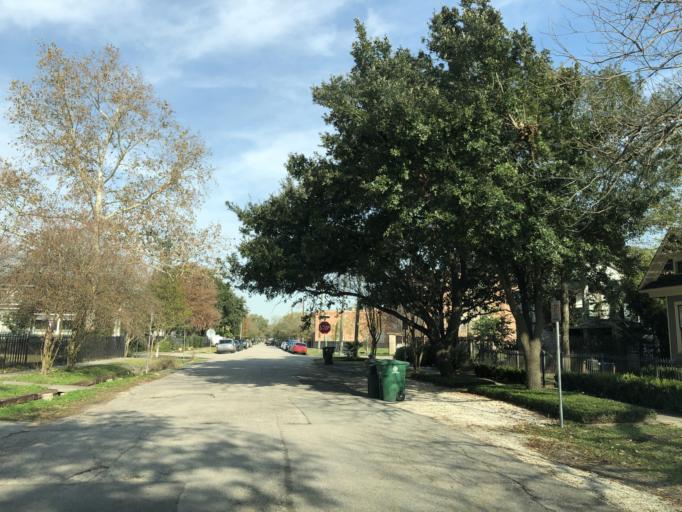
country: US
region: Texas
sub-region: Harris County
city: Houston
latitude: 29.7938
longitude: -95.3942
